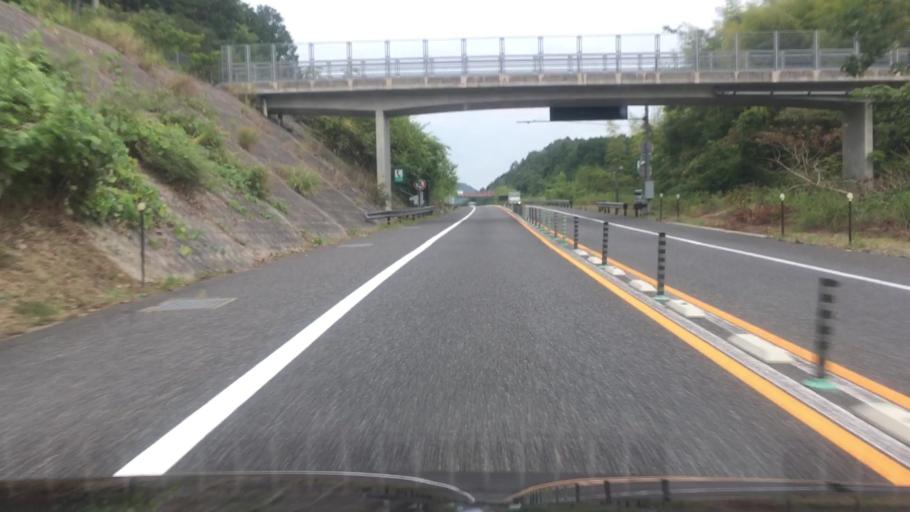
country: JP
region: Kyoto
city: Fukuchiyama
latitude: 35.1622
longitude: 135.0927
